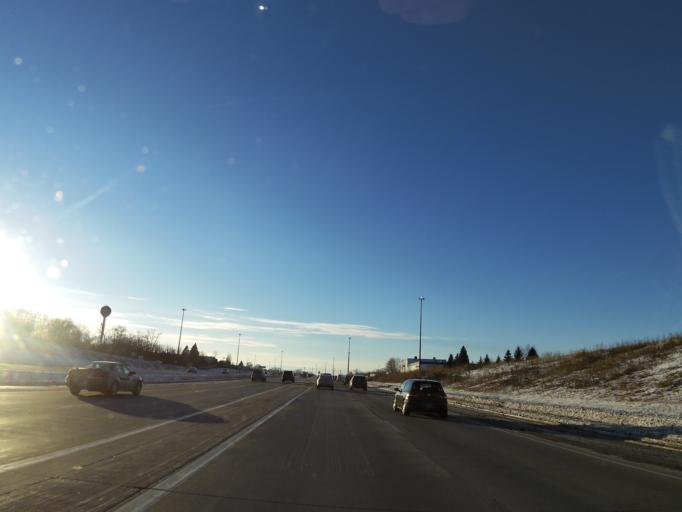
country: US
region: Minnesota
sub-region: Hennepin County
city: Eden Prairie
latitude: 44.8621
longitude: -93.4602
